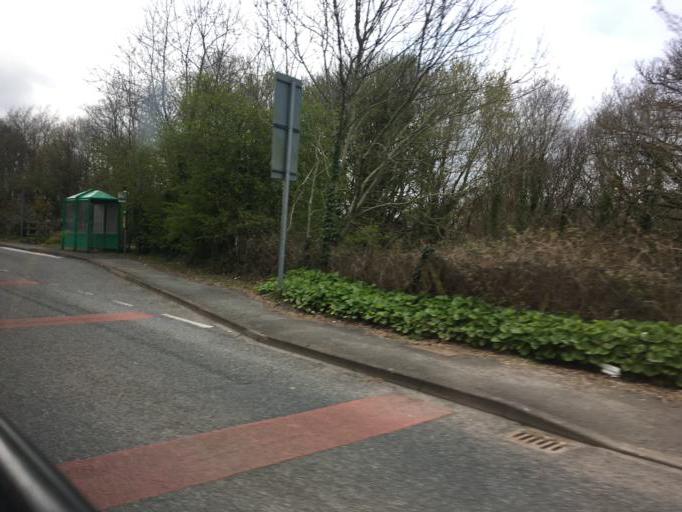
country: GB
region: Wales
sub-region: Gwynedd
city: Y Felinheli
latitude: 53.1748
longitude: -4.2241
